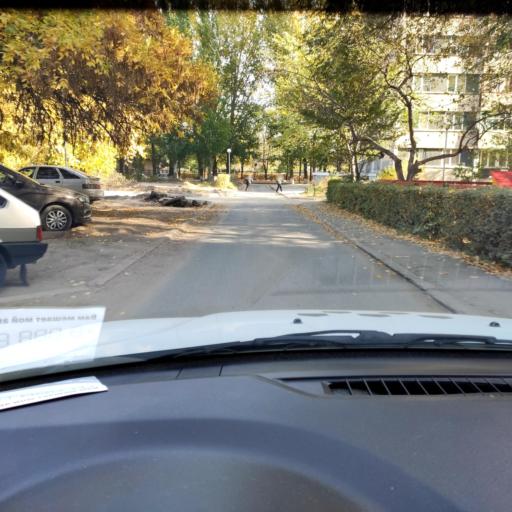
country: RU
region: Samara
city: Tol'yatti
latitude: 53.5173
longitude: 49.2649
